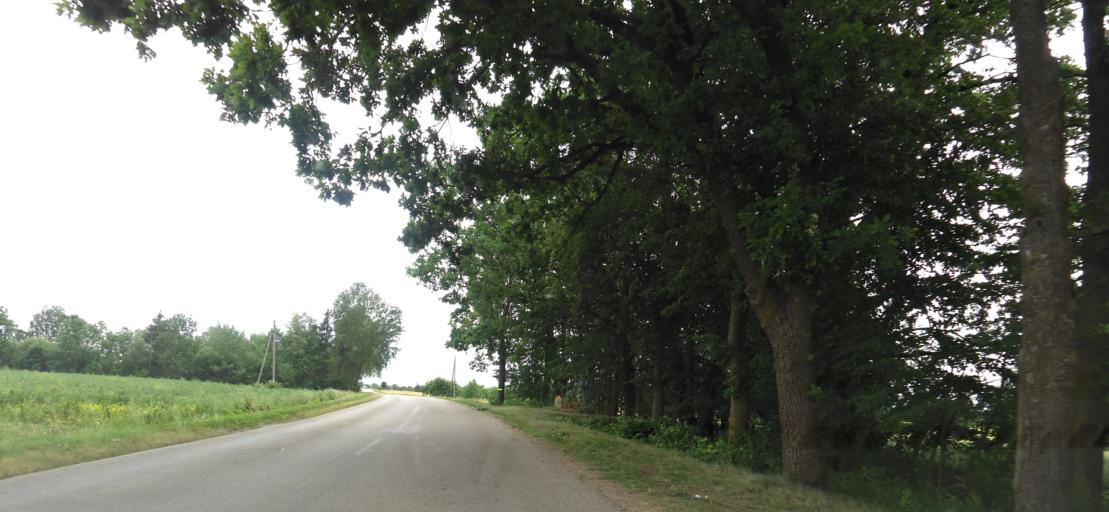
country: LT
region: Panevezys
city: Pasvalys
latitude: 56.0887
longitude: 24.4825
